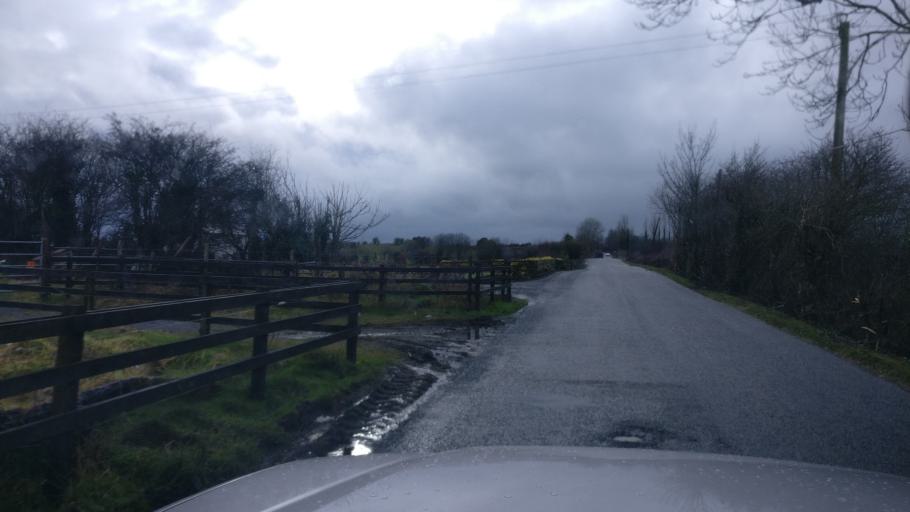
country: IE
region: Leinster
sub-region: An Iarmhi
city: Athlone
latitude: 53.4197
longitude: -8.0536
